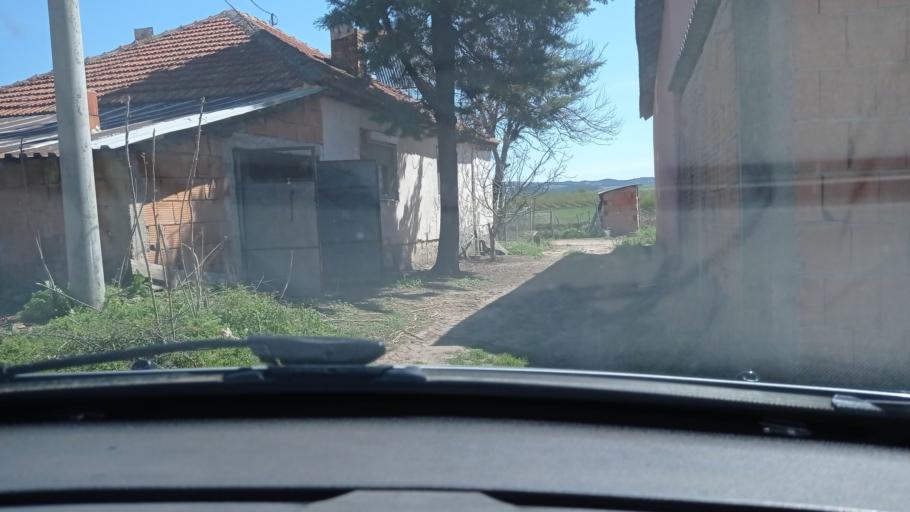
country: MK
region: Lozovo
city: Lozovo
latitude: 41.7620
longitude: 21.8713
